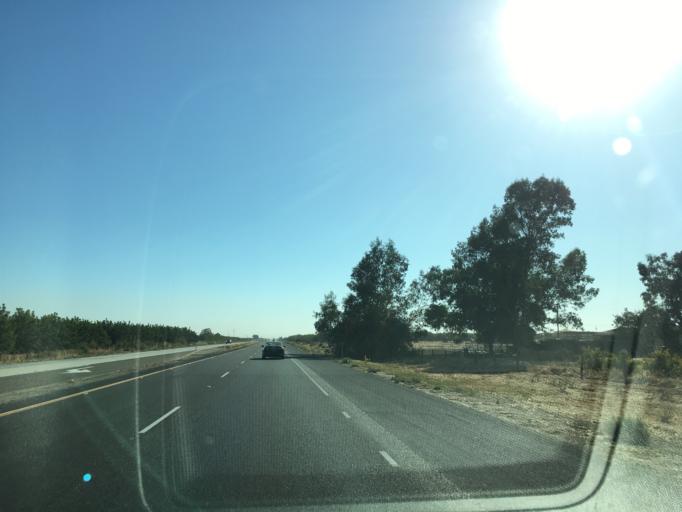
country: US
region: California
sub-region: Madera County
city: Chowchilla
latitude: 37.0834
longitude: -120.4368
